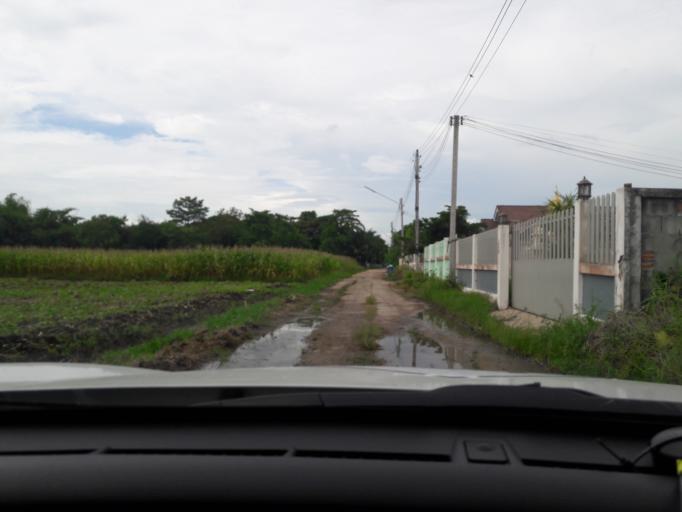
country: TH
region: Nakhon Sawan
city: Tak Fa
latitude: 15.3428
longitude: 100.5024
